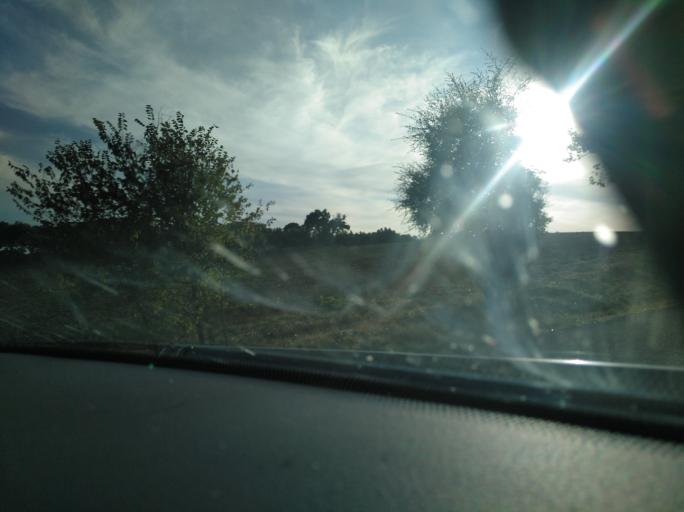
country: PT
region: Evora
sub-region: Estremoz
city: Estremoz
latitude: 38.9585
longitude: -7.5580
